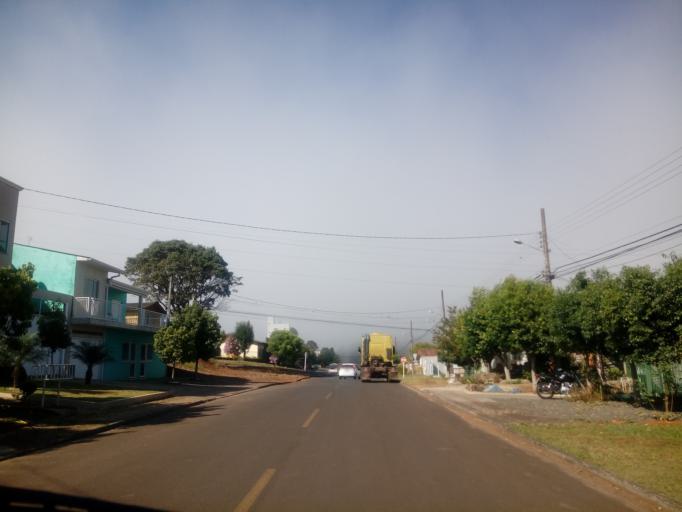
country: BR
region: Santa Catarina
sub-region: Chapeco
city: Chapeco
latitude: -27.0824
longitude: -52.6096
